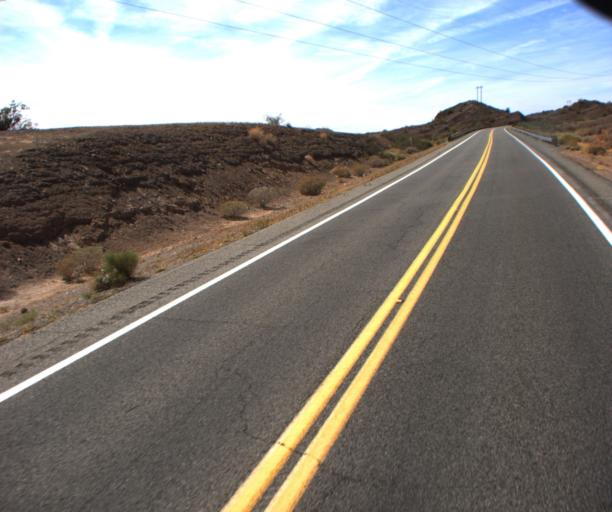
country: US
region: Arizona
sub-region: La Paz County
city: Cienega Springs
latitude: 34.3388
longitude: -114.1417
